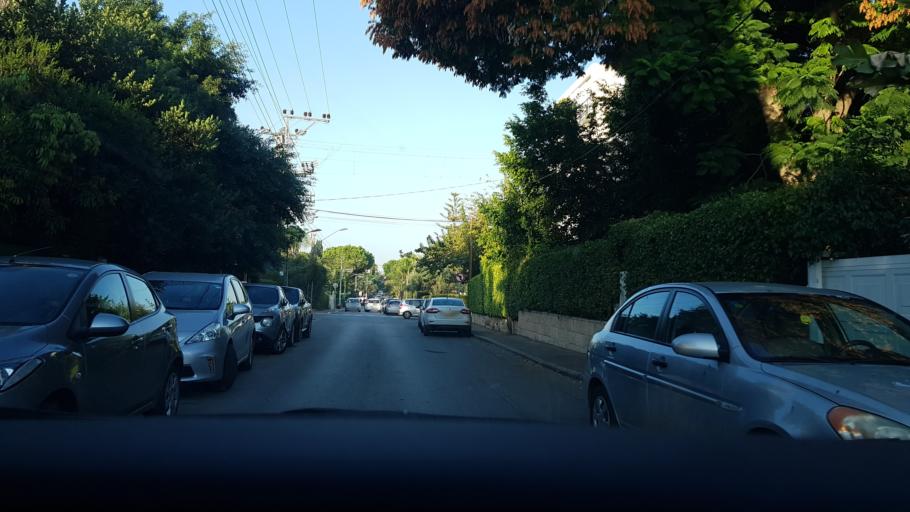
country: IL
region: Central District
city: Ness Ziona
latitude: 31.8968
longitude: 34.8230
